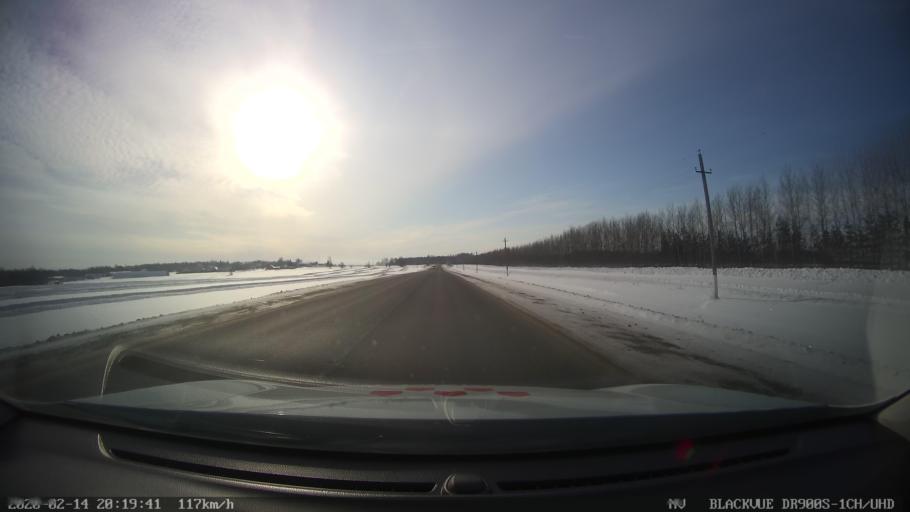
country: RU
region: Tatarstan
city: Verkhniy Uslon
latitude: 55.5673
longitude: 48.9014
